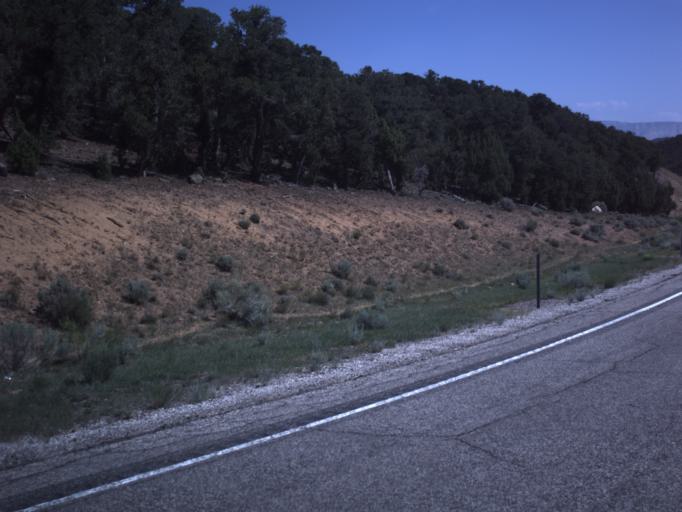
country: US
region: Utah
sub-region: Wayne County
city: Loa
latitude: 38.7162
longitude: -111.3996
